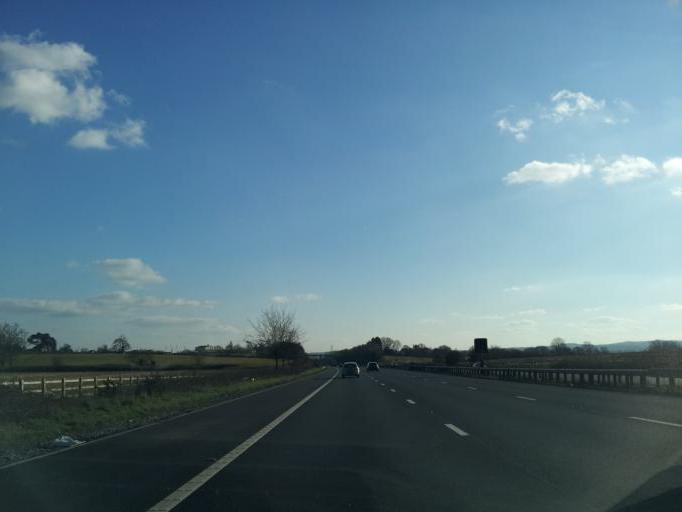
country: GB
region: England
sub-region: Devon
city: Cullompton
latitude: 50.8879
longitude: -3.3783
